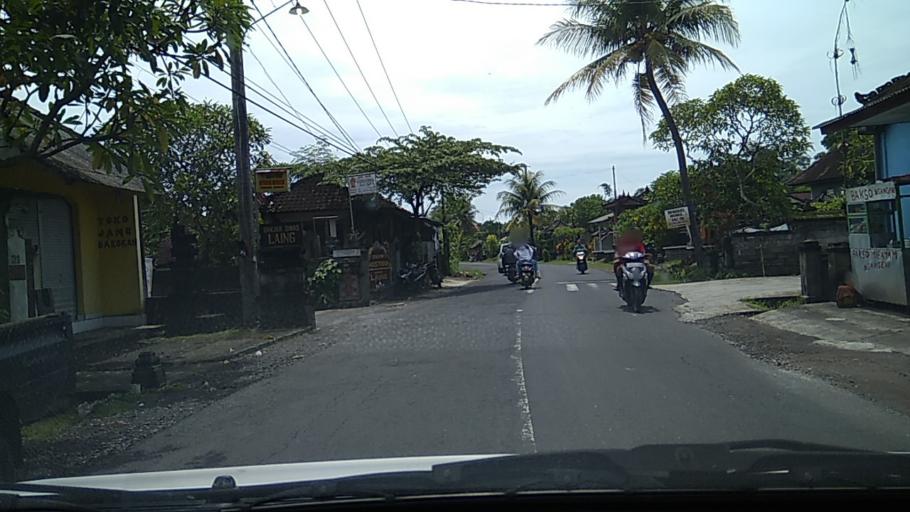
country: ID
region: Bali
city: Banjar Mundeh
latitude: -8.5751
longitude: 115.1386
